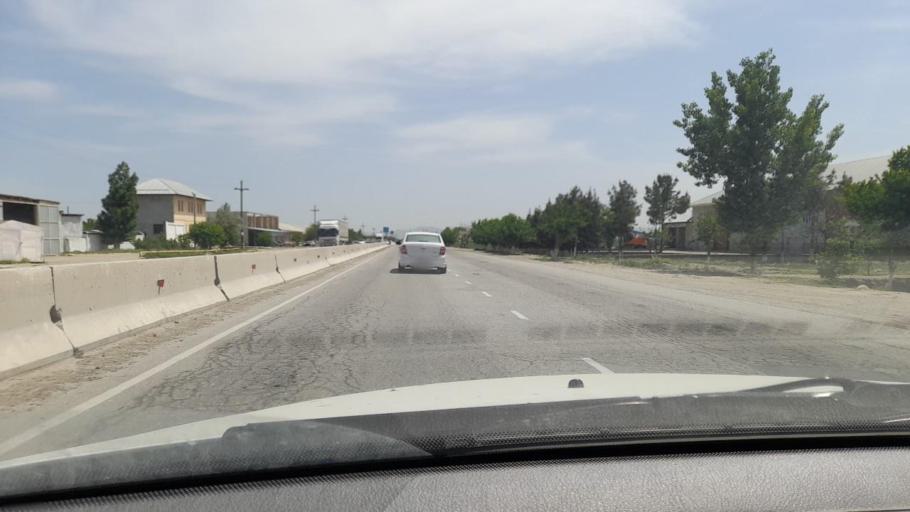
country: UZ
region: Navoiy
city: Karmana Shahri
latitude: 40.1366
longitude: 65.4029
